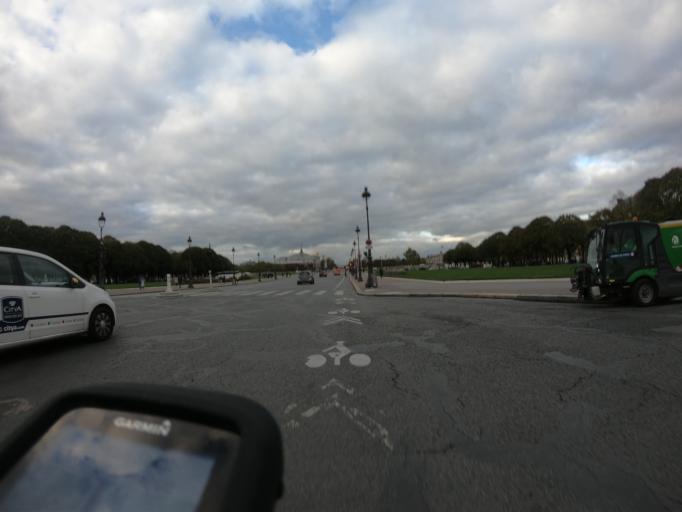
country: FR
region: Ile-de-France
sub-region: Paris
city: Paris
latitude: 48.8600
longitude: 2.3133
